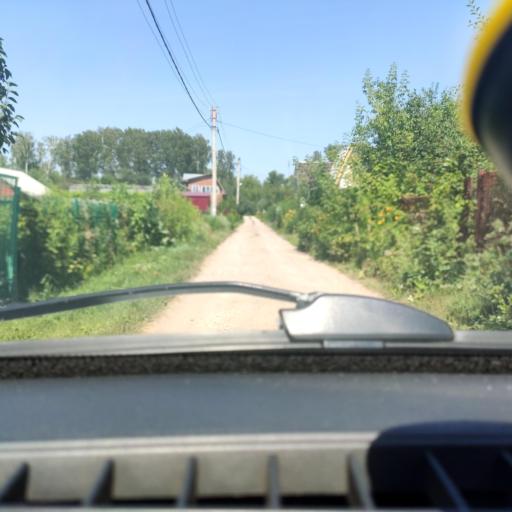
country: RU
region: Samara
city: Tol'yatti
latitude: 53.5977
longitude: 49.3053
